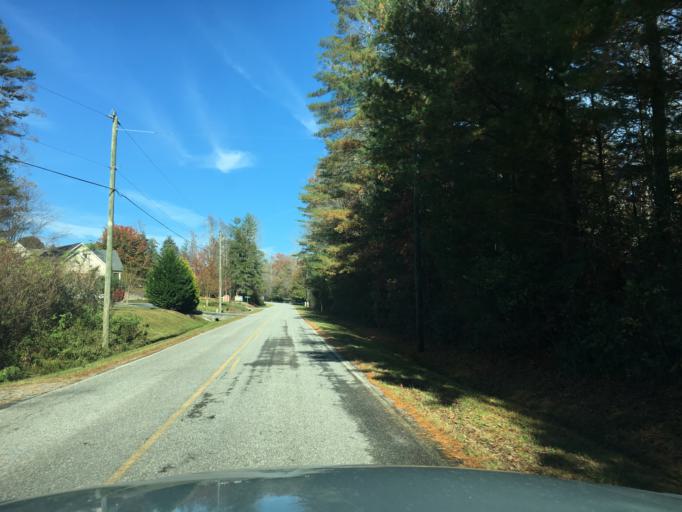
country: US
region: North Carolina
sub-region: Henderson County
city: Etowah
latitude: 35.3225
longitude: -82.6167
